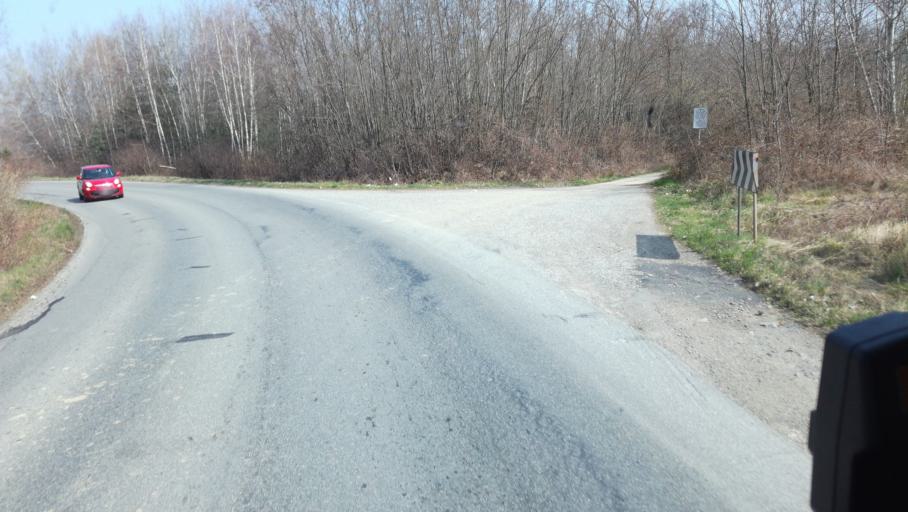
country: IT
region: Piedmont
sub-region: Provincia di Novara
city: Romagnano Sesia
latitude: 45.6345
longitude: 8.4025
